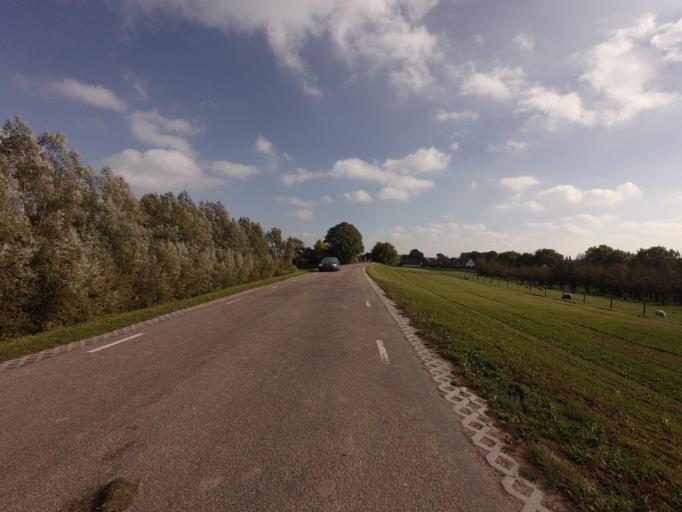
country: NL
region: Gelderland
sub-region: Gemeente Culemborg
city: Culemborg
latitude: 51.9559
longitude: 5.2792
